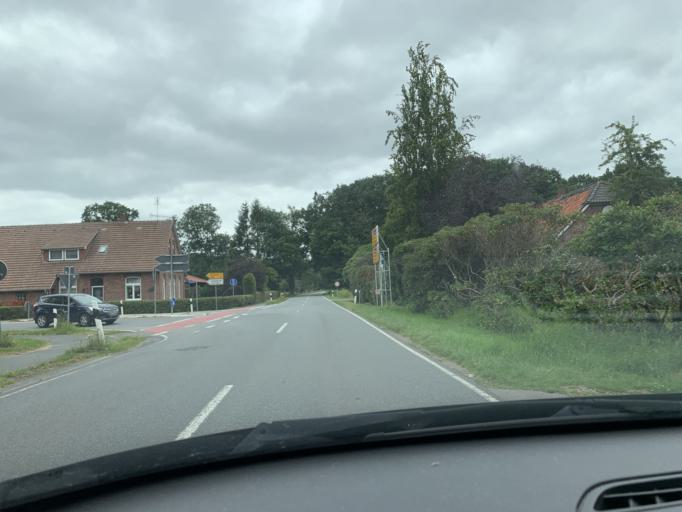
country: DE
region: Lower Saxony
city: Bad Zwischenahn
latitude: 53.2215
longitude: 8.0130
